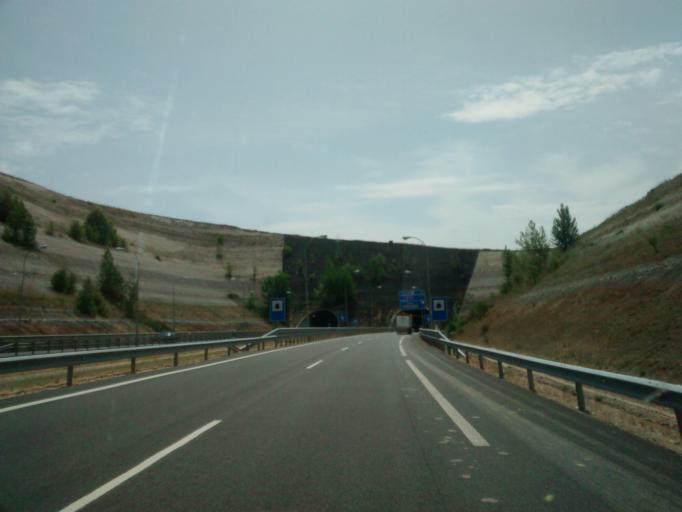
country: ES
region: Castille and Leon
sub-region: Provincia de Burgos
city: Tardajos
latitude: 42.3580
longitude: -3.8019
